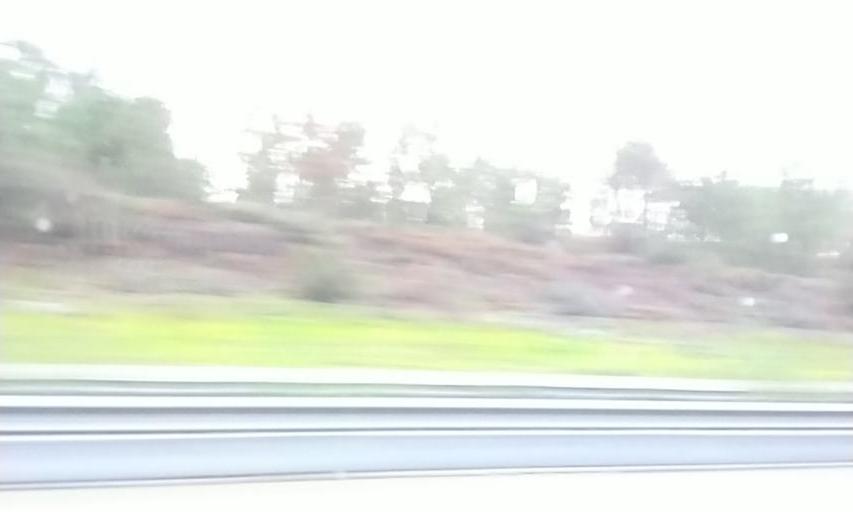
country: PT
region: Braga
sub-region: Barcelos
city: Galegos
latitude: 41.6016
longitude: -8.5518
